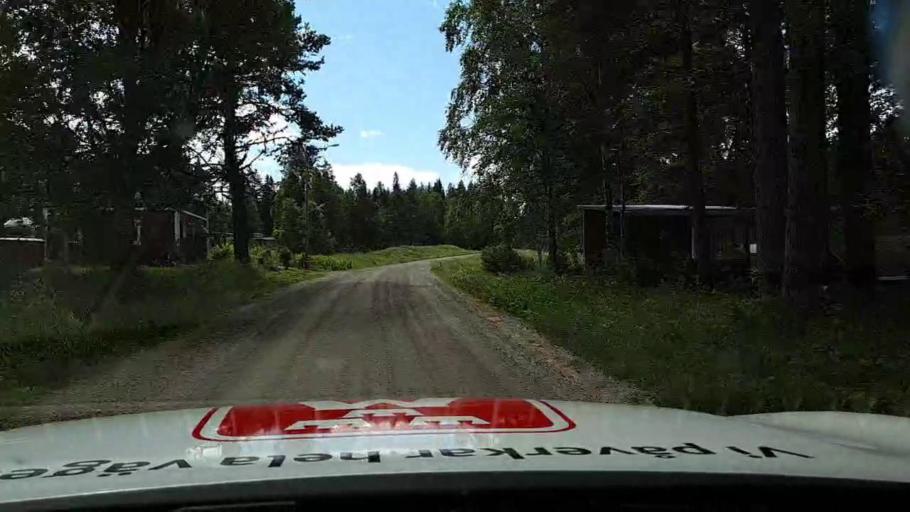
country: SE
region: Jaemtland
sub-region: Braecke Kommun
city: Braecke
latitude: 62.7498
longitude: 15.5028
